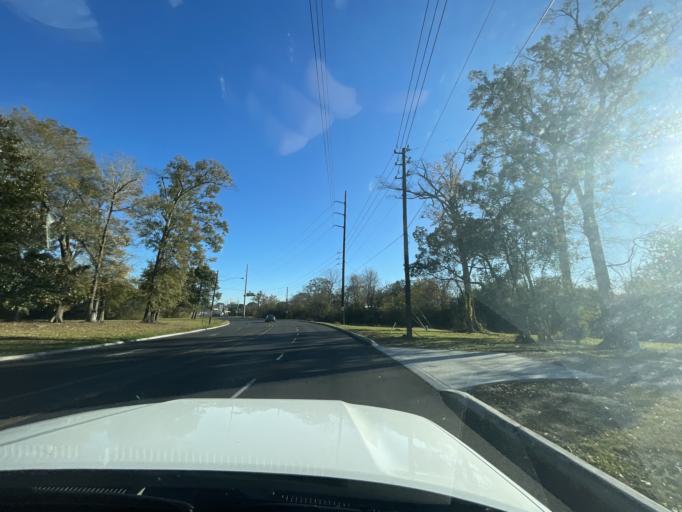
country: US
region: Louisiana
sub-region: East Baton Rouge Parish
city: Baton Rouge
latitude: 30.4287
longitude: -91.1527
